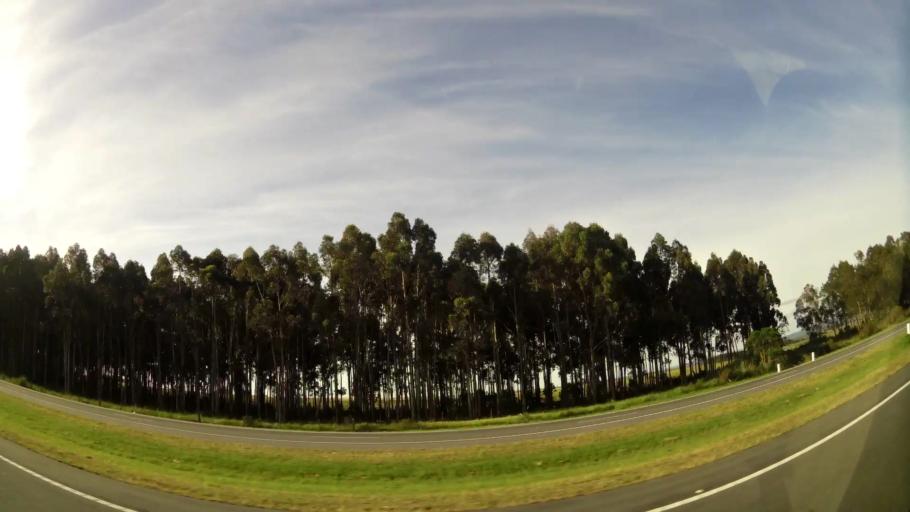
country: UY
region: Lavalleja
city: Solis de Mataojo
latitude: -34.7802
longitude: -55.4735
